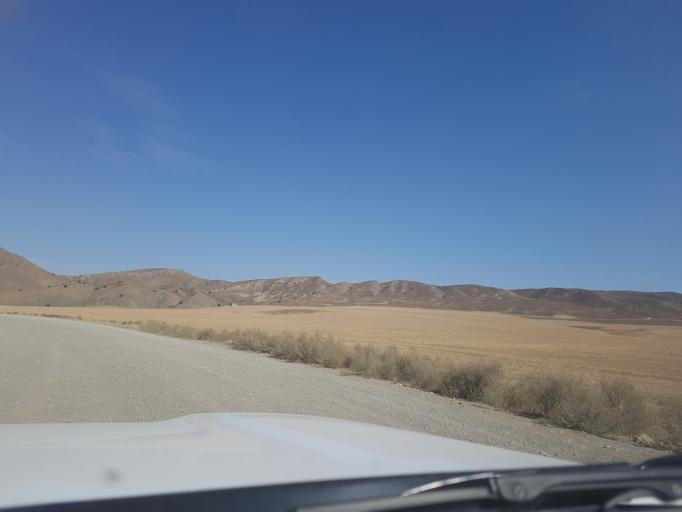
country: TM
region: Ahal
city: Baharly
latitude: 38.4357
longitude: 57.0395
